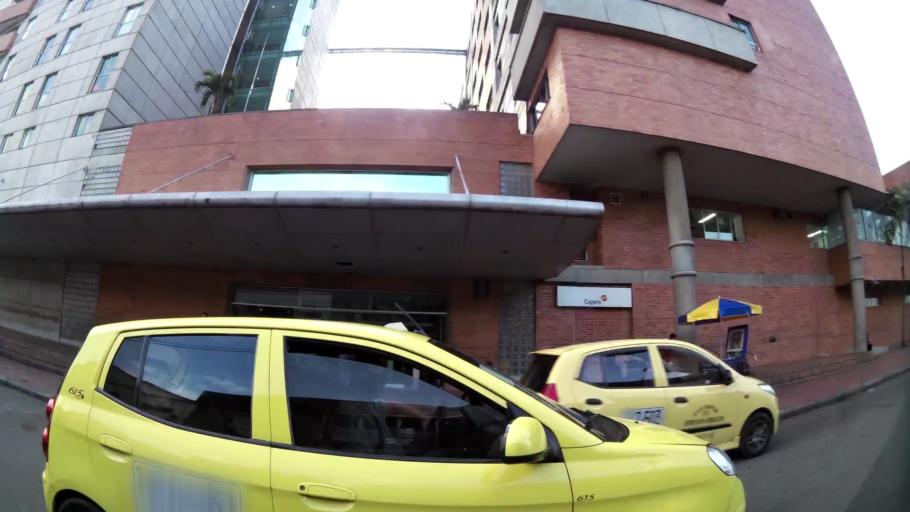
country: CO
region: Antioquia
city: Medellin
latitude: 6.2347
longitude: -75.5729
